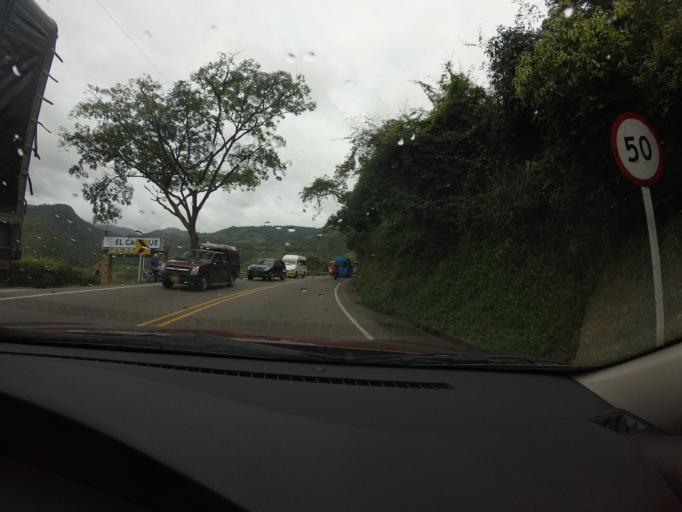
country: CO
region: Cundinamarca
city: Guaduas
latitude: 5.0646
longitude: -74.5876
